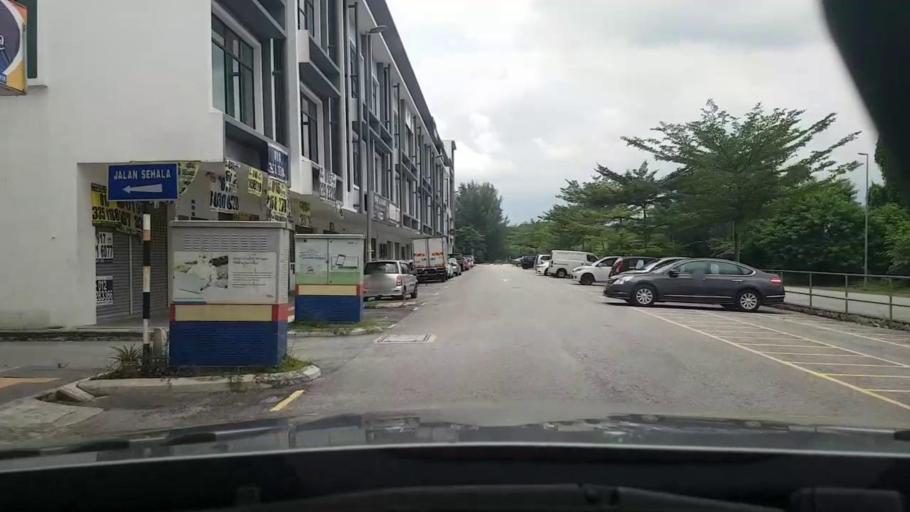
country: MY
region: Selangor
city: Subang Jaya
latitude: 2.9857
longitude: 101.6196
